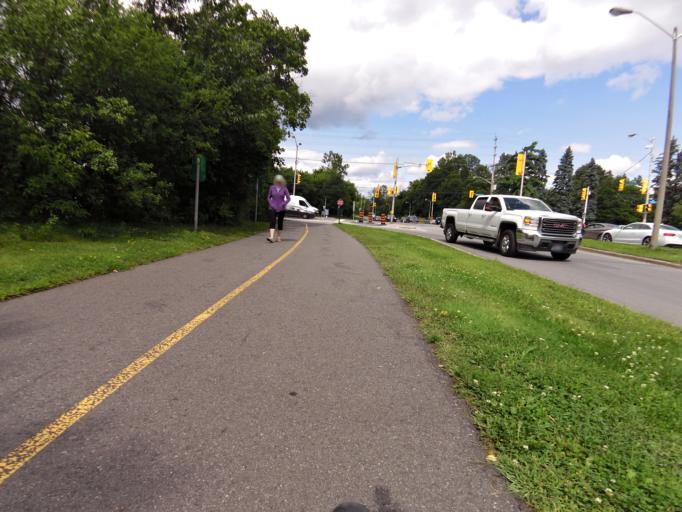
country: CA
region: Ontario
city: Ottawa
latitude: 45.4432
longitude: -75.6390
